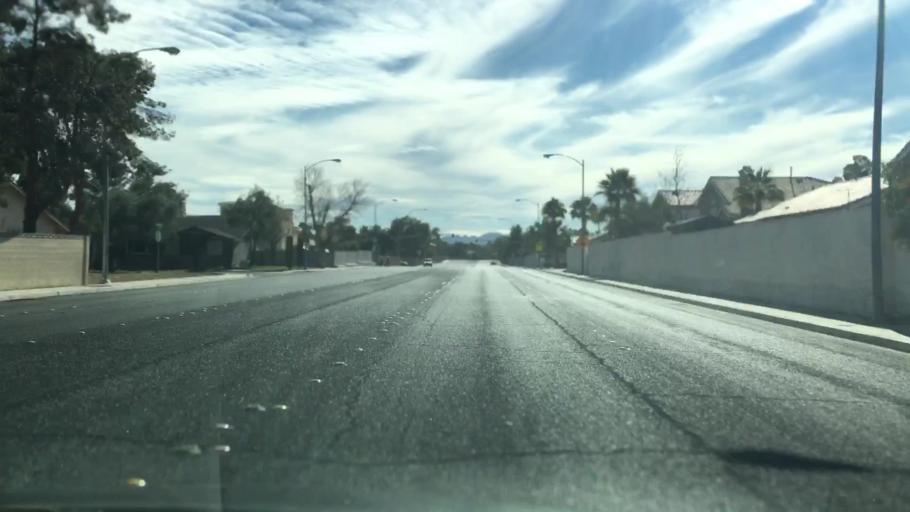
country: US
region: Nevada
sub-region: Clark County
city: Paradise
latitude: 36.0516
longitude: -115.1408
